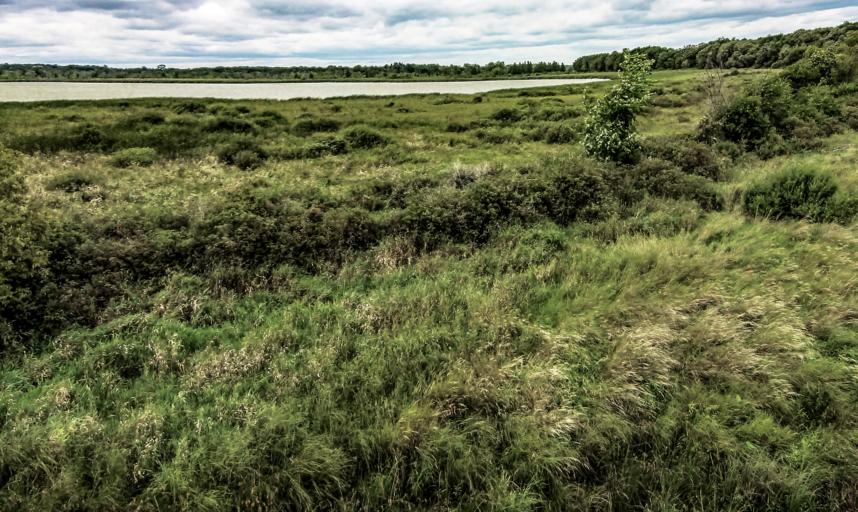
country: US
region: Wisconsin
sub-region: Jefferson County
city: Lake Mills
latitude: 43.0464
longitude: -88.9156
